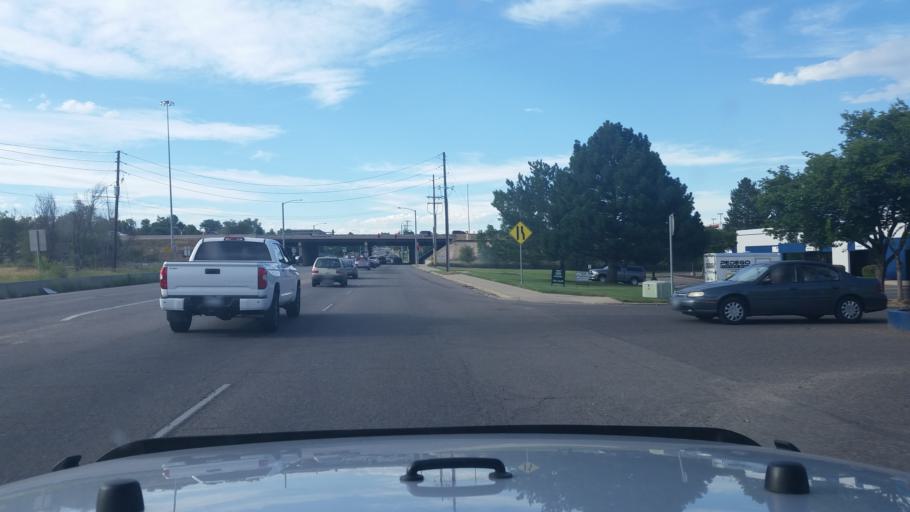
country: US
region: Colorado
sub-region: Adams County
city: Twin Lakes
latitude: 39.8258
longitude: -104.9873
